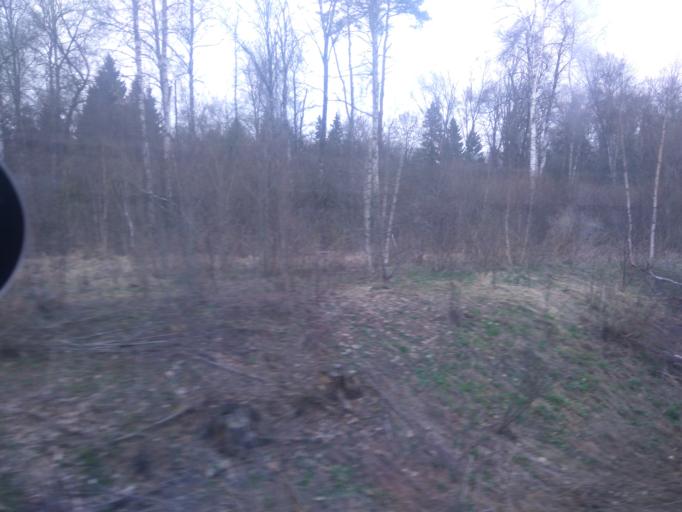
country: RU
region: Moskovskaya
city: Svatkovo
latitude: 56.3622
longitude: 38.2085
